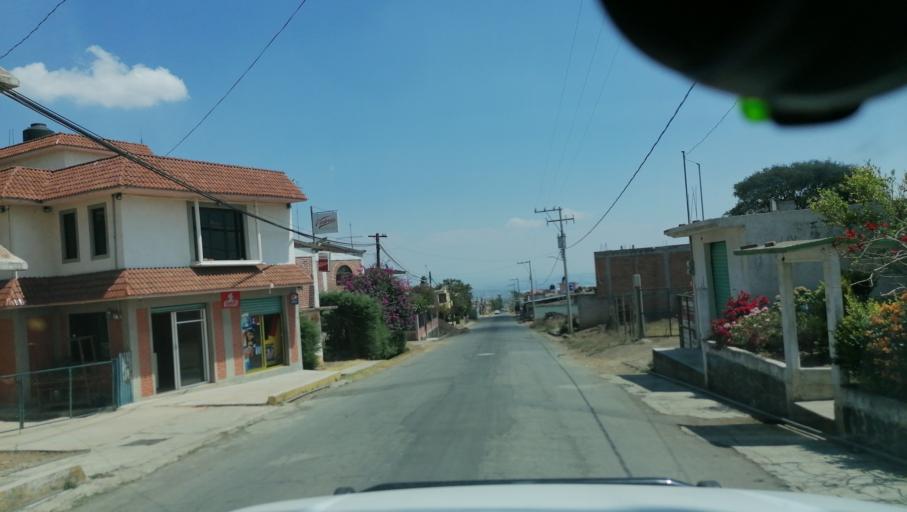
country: MX
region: Puebla
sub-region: Chiautzingo
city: San Nicolas Zecalacoayan
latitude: 19.1746
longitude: -98.4941
